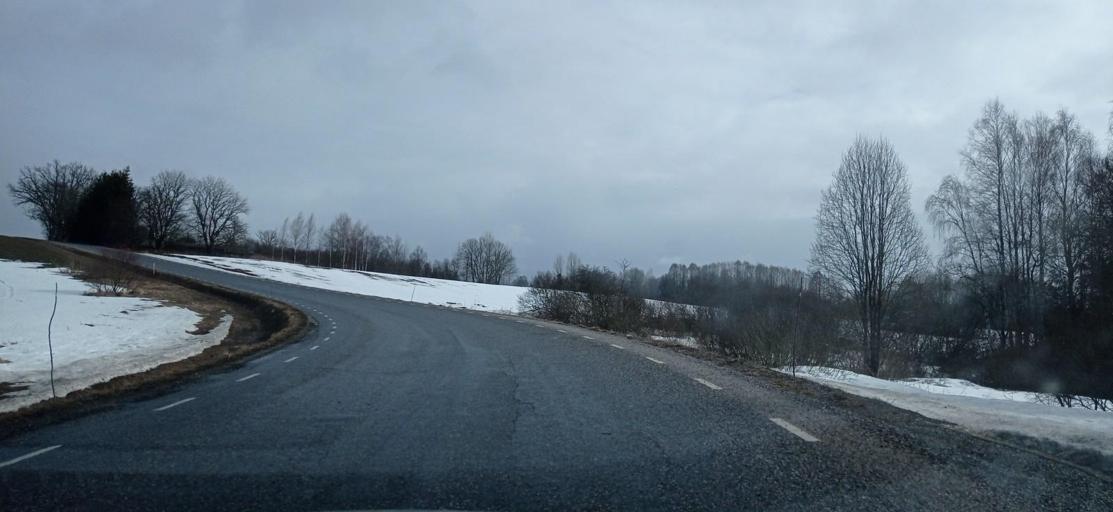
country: EE
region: Tartu
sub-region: UElenurme vald
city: Ulenurme
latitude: 58.0788
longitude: 26.6824
